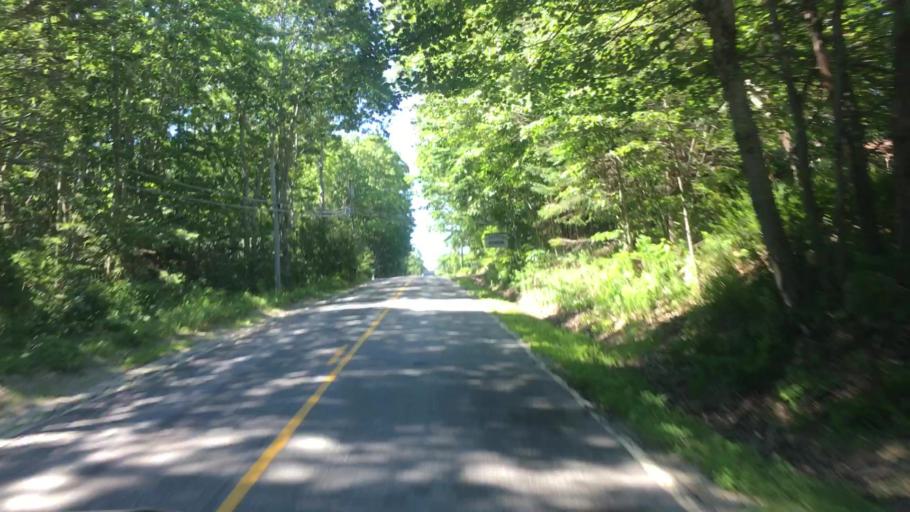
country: US
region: Maine
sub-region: Hancock County
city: Sedgwick
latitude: 44.3210
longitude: -68.6092
